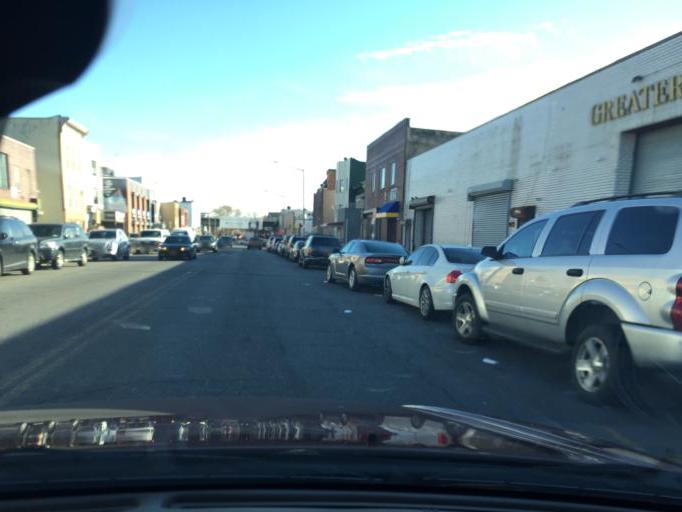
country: US
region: New York
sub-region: Kings County
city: Bensonhurst
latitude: 40.6287
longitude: -73.9984
